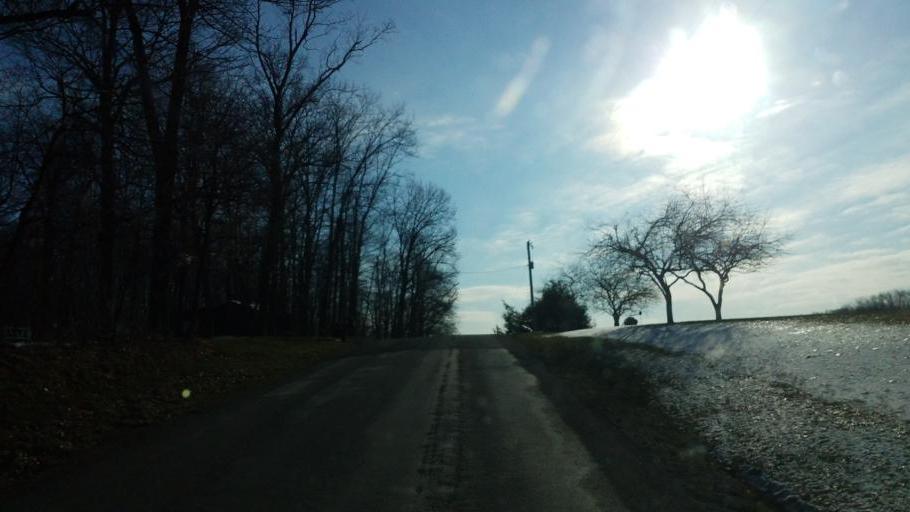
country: US
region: Ohio
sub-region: Sandusky County
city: Bellville
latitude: 40.6092
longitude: -82.5556
